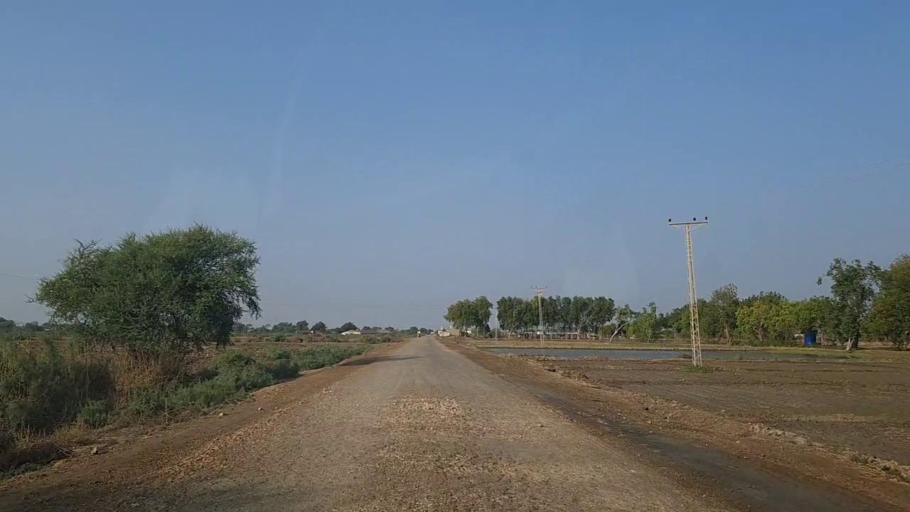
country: PK
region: Sindh
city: Mirpur Sakro
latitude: 24.5665
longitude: 67.6700
